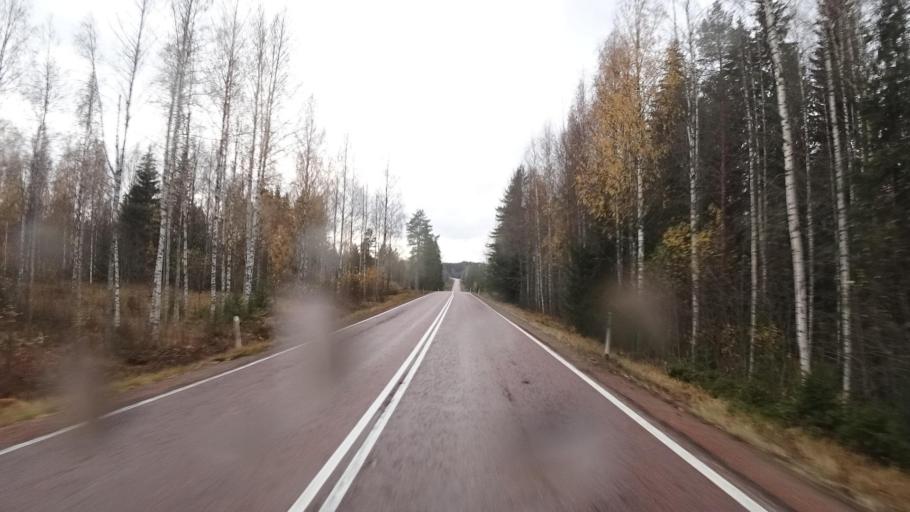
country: FI
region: Southern Savonia
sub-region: Mikkeli
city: Kangasniemi
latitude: 62.0707
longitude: 26.6691
